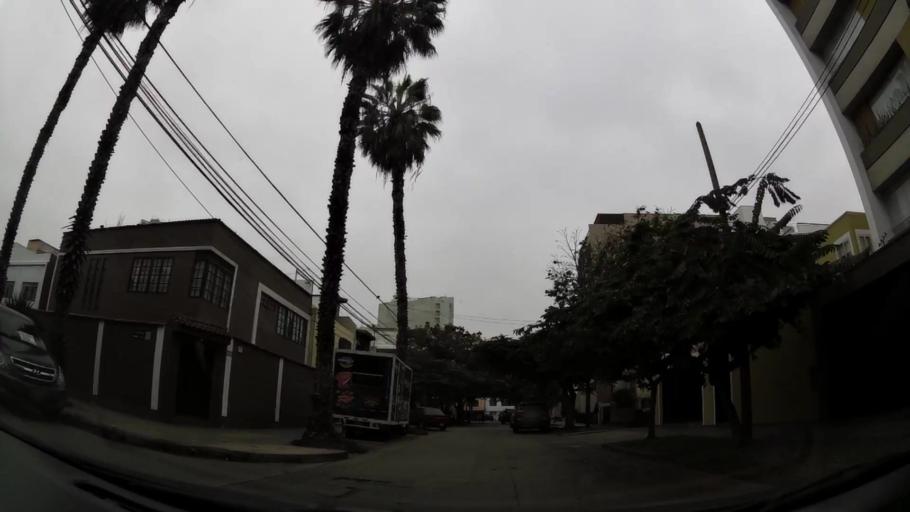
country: PE
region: Lima
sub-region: Lima
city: Surco
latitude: -12.1400
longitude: -77.0255
